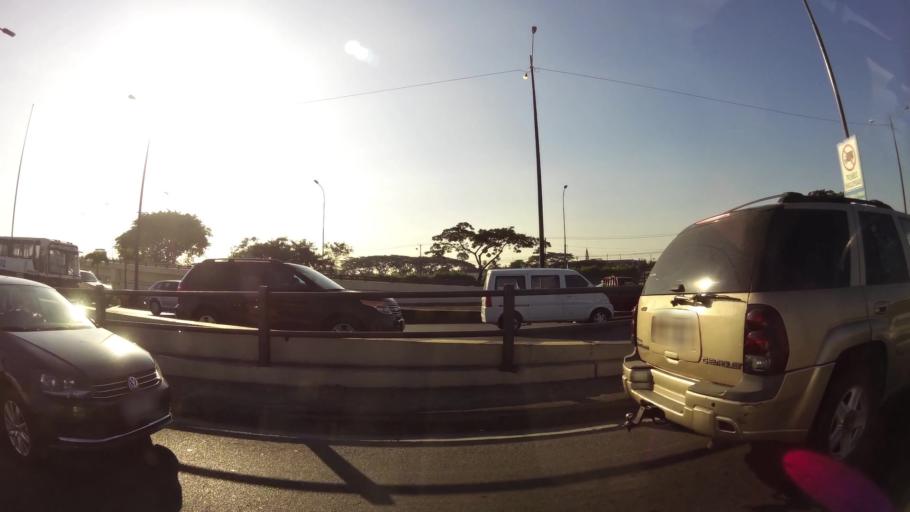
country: EC
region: Guayas
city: Eloy Alfaro
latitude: -2.1567
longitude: -79.8805
